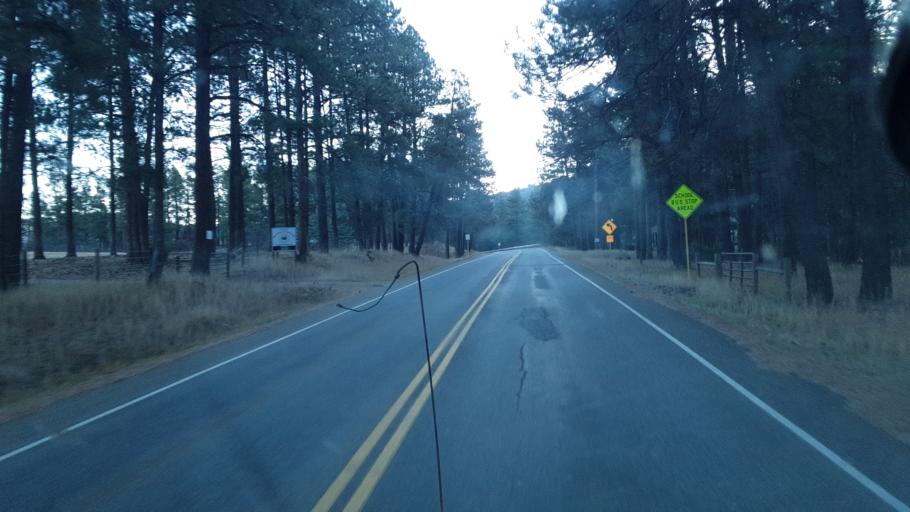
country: US
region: Colorado
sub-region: La Plata County
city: Durango
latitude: 37.3310
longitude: -107.7341
